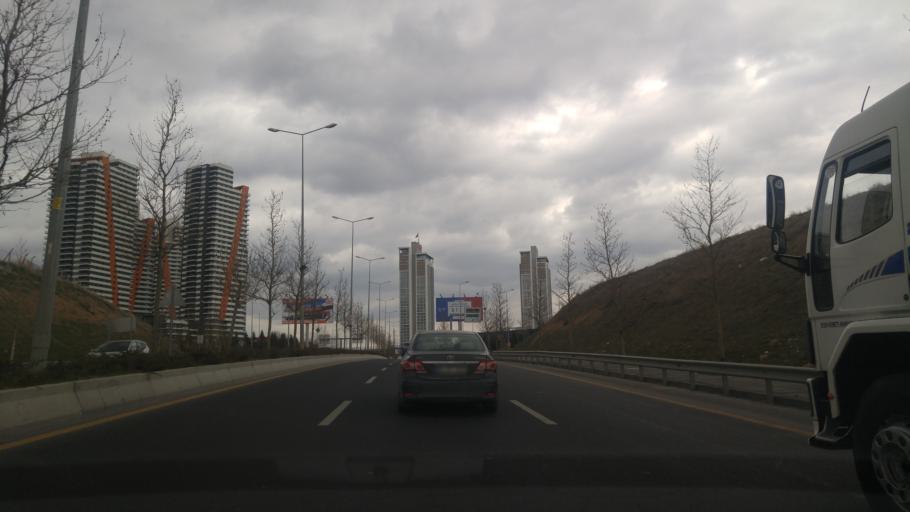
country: TR
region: Ankara
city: Mamak
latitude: 39.8868
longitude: 32.9270
